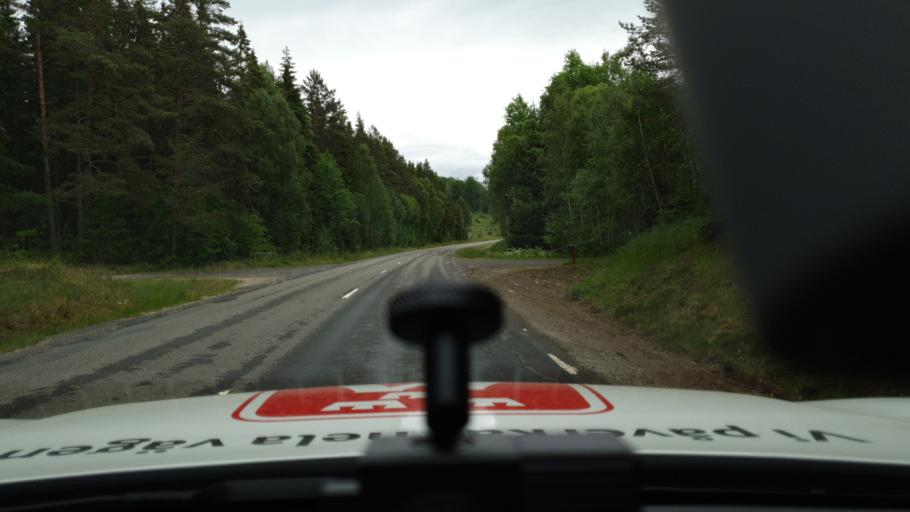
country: SE
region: Joenkoeping
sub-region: Mullsjo Kommun
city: Mullsjoe
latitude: 57.9871
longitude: 13.7901
